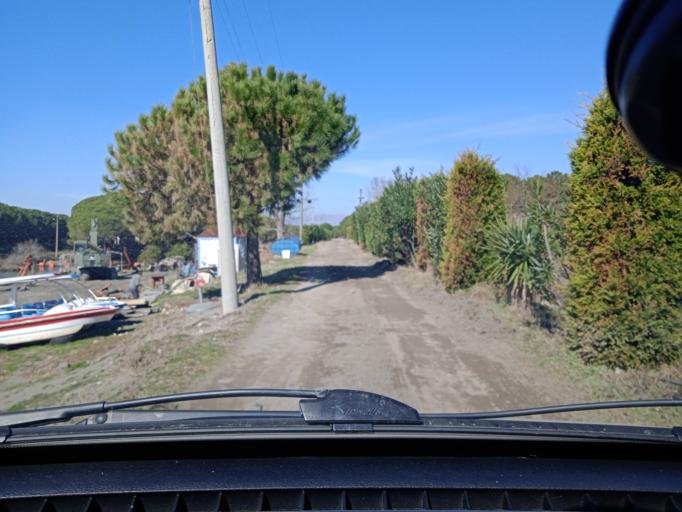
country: AL
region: Shkoder
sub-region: Rrethi i Shkodres
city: Velipoje
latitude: 41.8616
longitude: 19.4462
